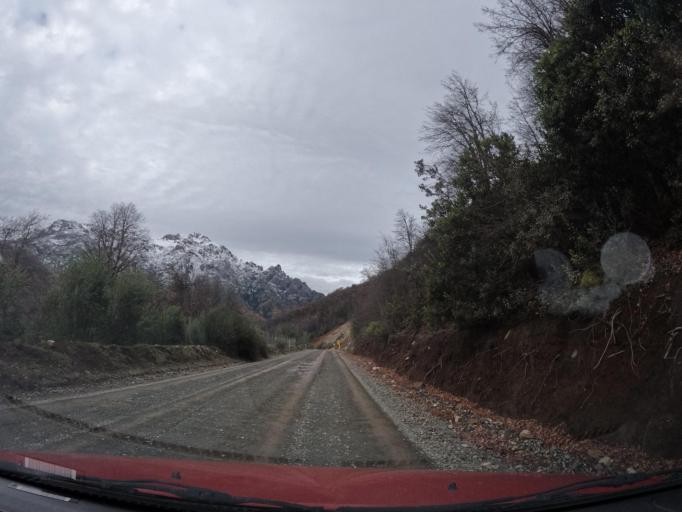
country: CL
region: Maule
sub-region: Provincia de Linares
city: Colbun
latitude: -35.8586
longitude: -71.1458
